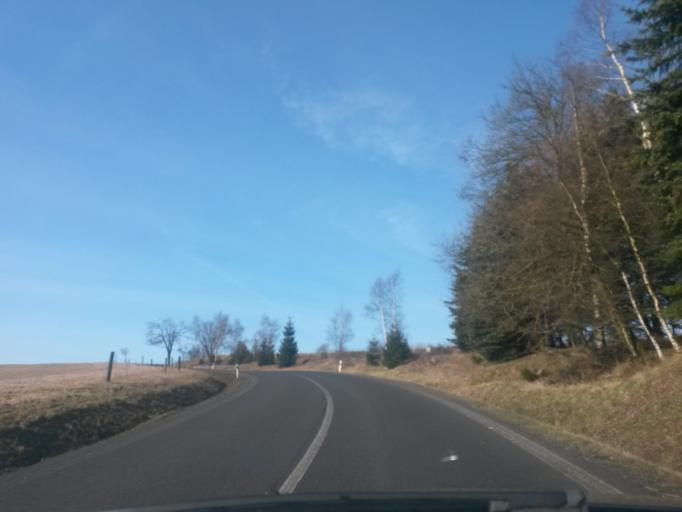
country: CZ
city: Krasna Lipa
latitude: 50.4792
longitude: 13.2673
